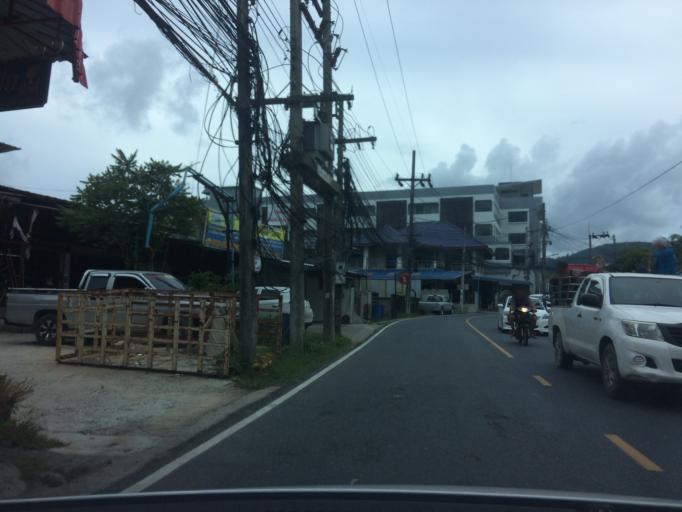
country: TH
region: Phuket
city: Mueang Phuket
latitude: 7.8624
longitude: 98.3606
